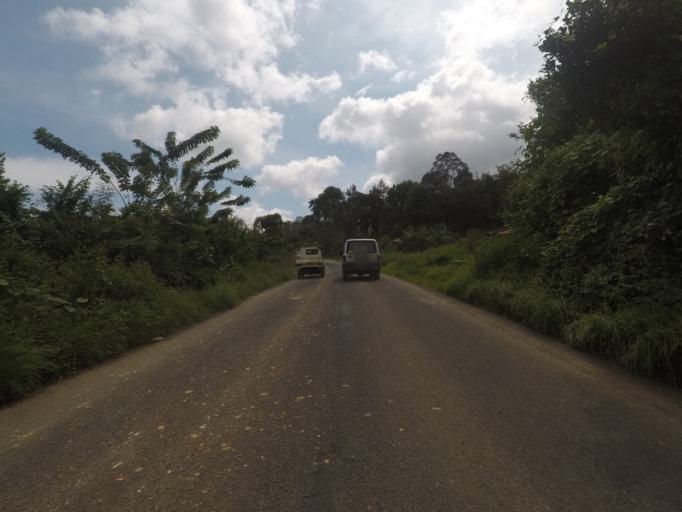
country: IN
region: Karnataka
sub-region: Kodagu
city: Virarajendrapet
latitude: 12.2340
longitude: 75.8461
